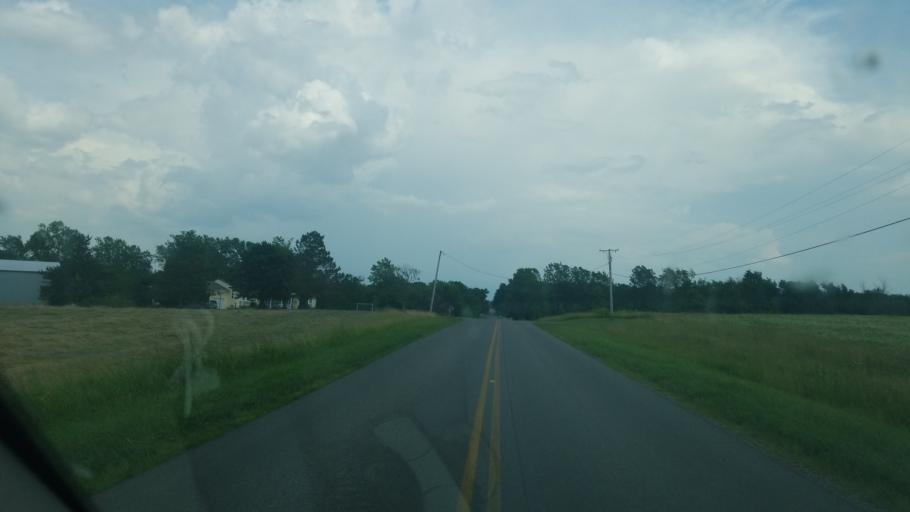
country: US
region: Ohio
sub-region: Logan County
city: Northwood
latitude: 40.4652
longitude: -83.6879
